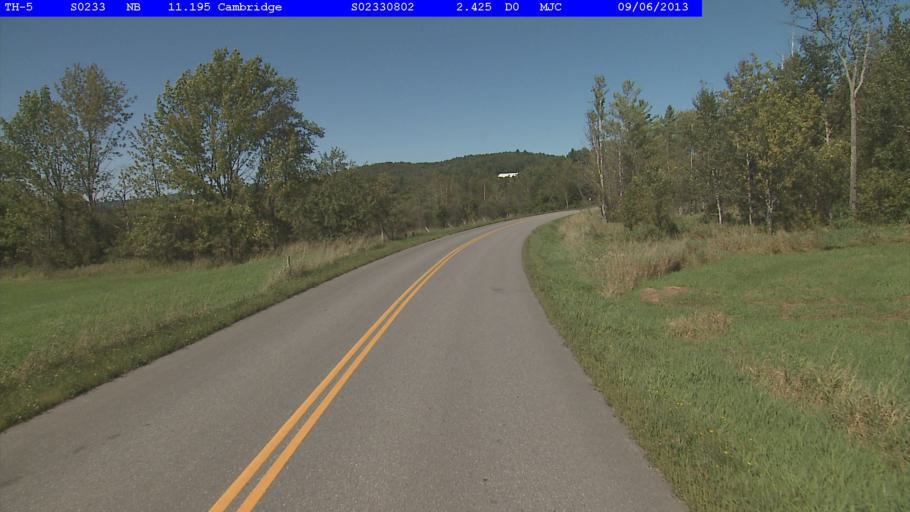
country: US
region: Vermont
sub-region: Lamoille County
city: Johnson
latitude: 44.6166
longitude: -72.8579
